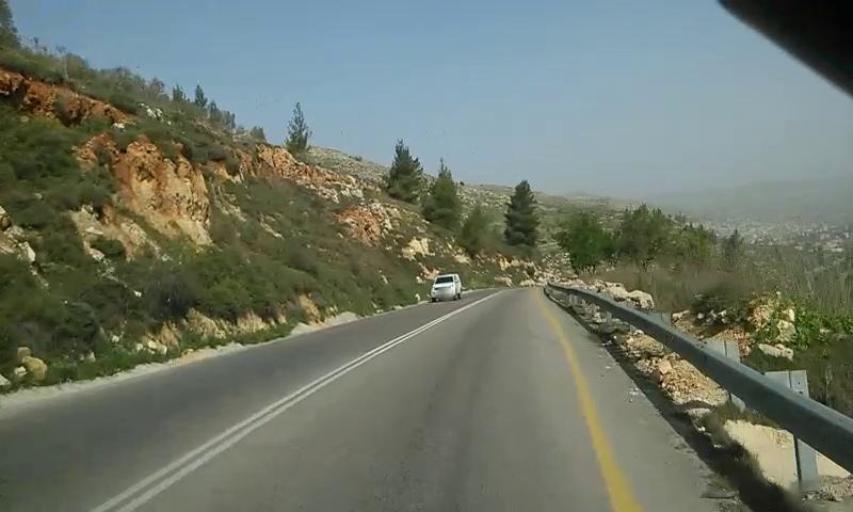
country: PS
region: West Bank
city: Yatma
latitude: 32.1225
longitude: 35.2559
